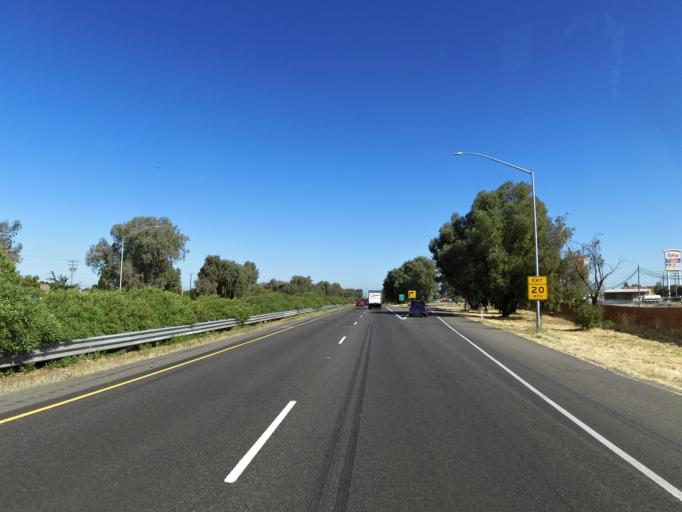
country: US
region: California
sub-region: Sacramento County
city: Galt
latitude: 38.2878
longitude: -121.3100
